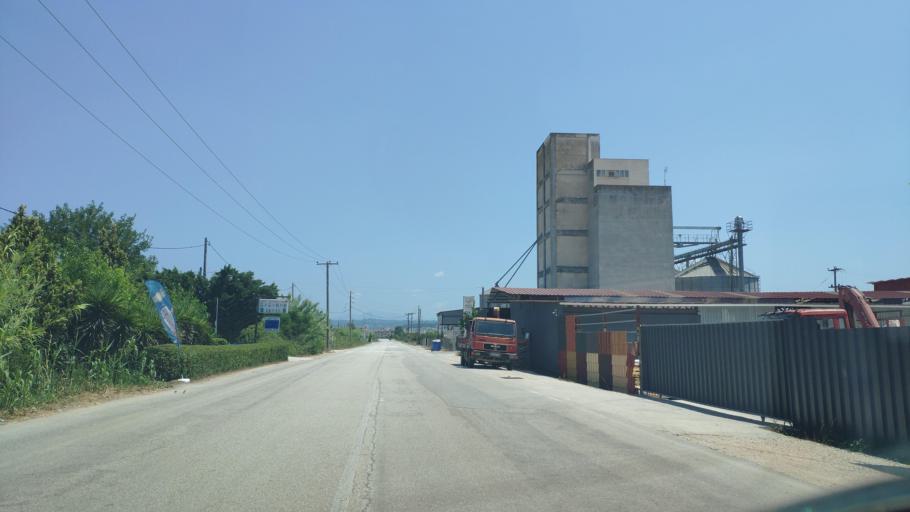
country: GR
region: Epirus
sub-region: Nomos Artas
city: Kostakioi
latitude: 39.1276
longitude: 20.9453
